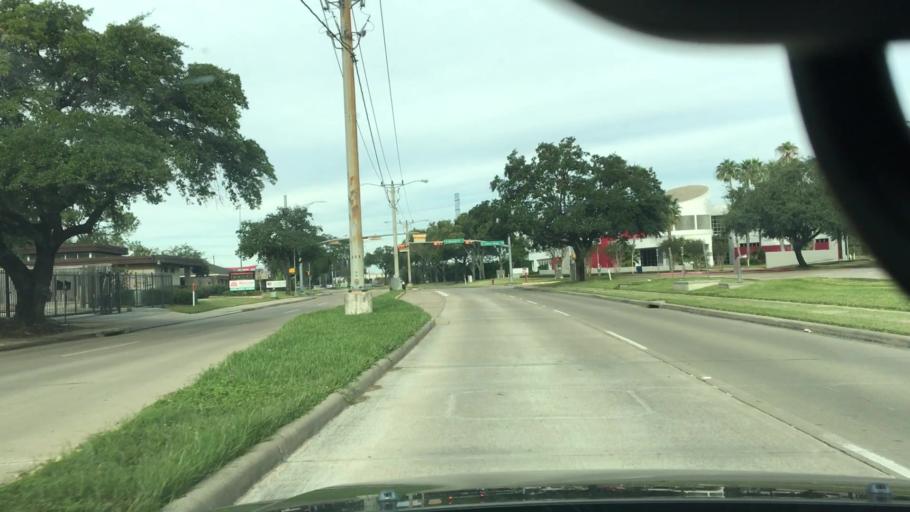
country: US
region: Texas
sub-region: Harris County
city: Webster
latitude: 29.5491
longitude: -95.1092
